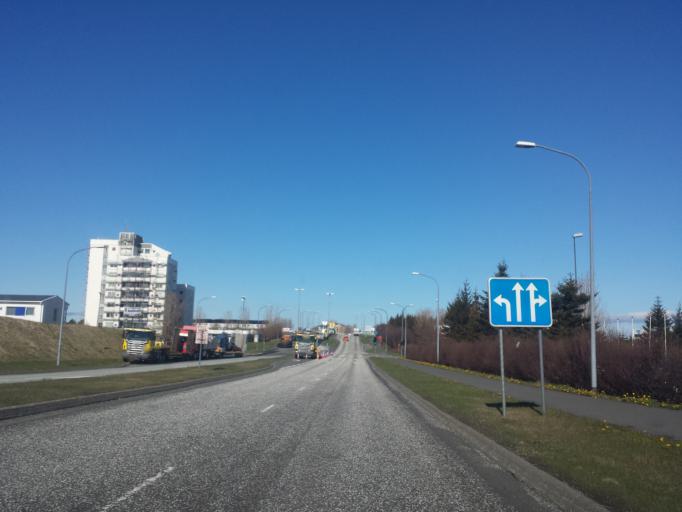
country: IS
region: Capital Region
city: Reykjavik
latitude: 64.1200
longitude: -21.8053
